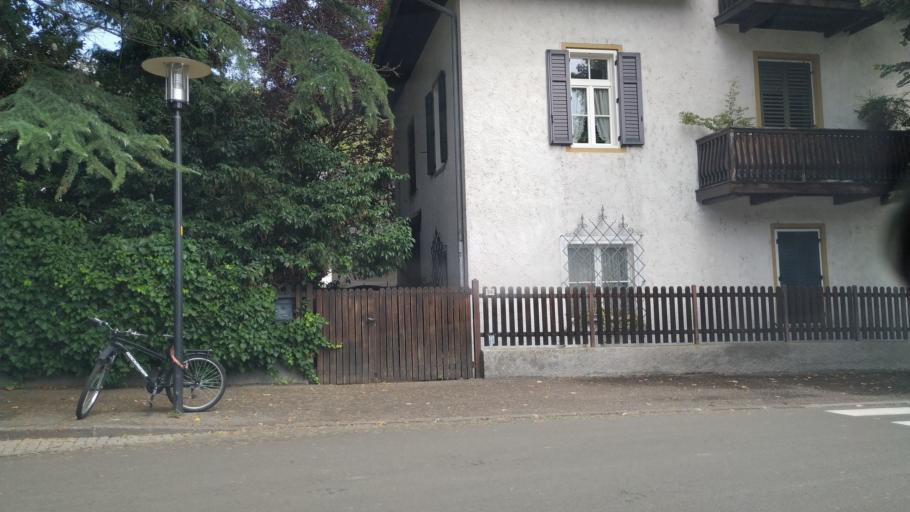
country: IT
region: Trentino-Alto Adige
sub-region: Bolzano
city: Tirolo
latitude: 46.6825
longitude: 11.1470
